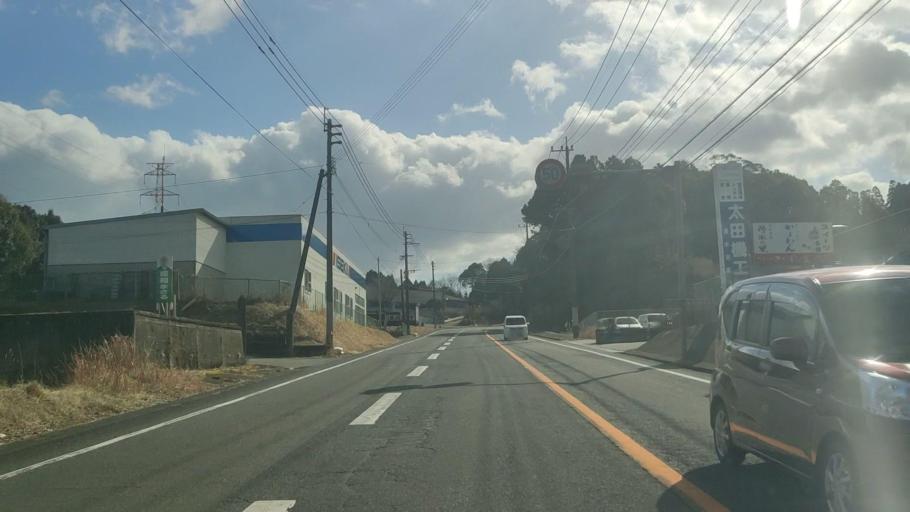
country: JP
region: Kagoshima
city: Okuchi-shinohara
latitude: 31.9307
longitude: 130.7034
